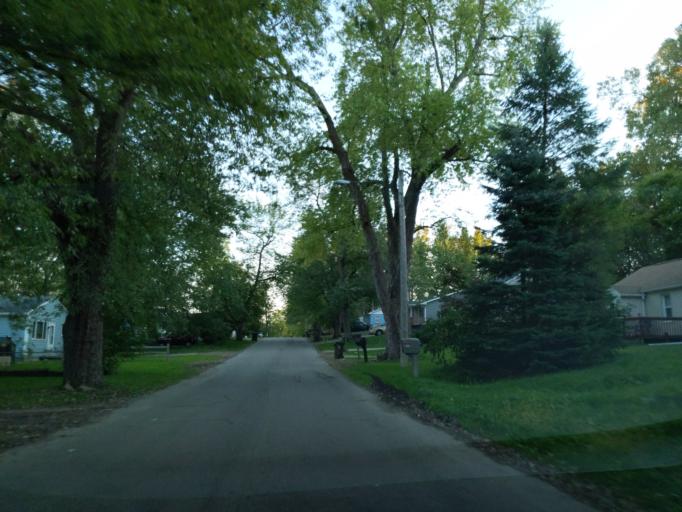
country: US
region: Michigan
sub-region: Ingham County
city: Edgemont Park
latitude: 42.7355
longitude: -84.5911
